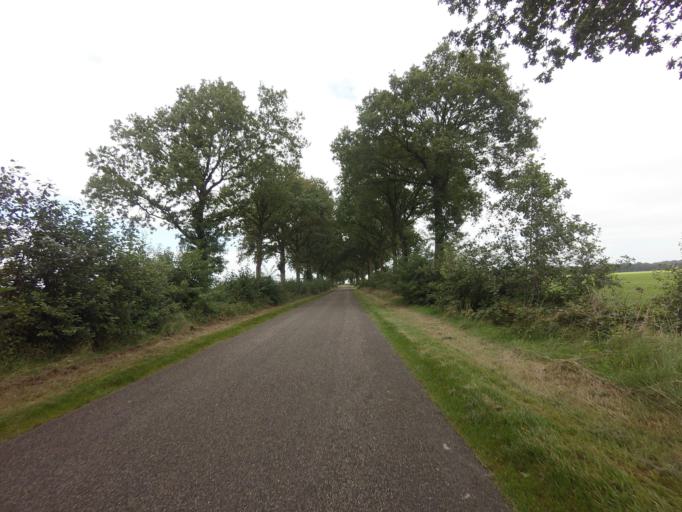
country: NL
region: Drenthe
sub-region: Gemeente Westerveld
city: Dwingeloo
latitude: 52.9709
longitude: 6.3591
